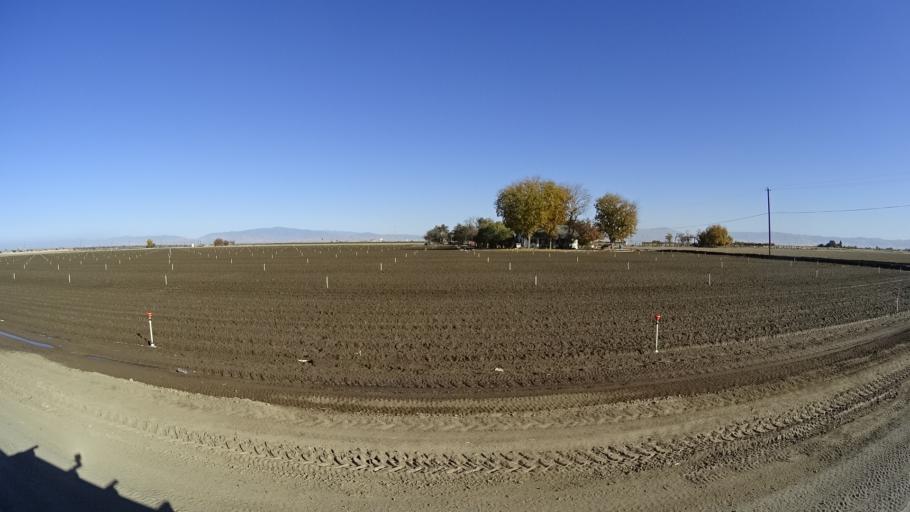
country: US
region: California
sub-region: Kern County
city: Greenacres
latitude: 35.2779
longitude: -119.1105
